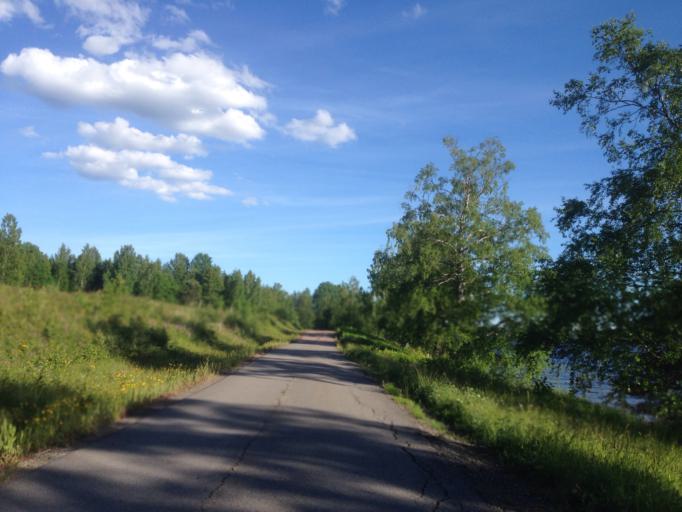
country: SE
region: Dalarna
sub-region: Ludvika Kommun
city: Ludvika
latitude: 60.1131
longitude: 15.2051
